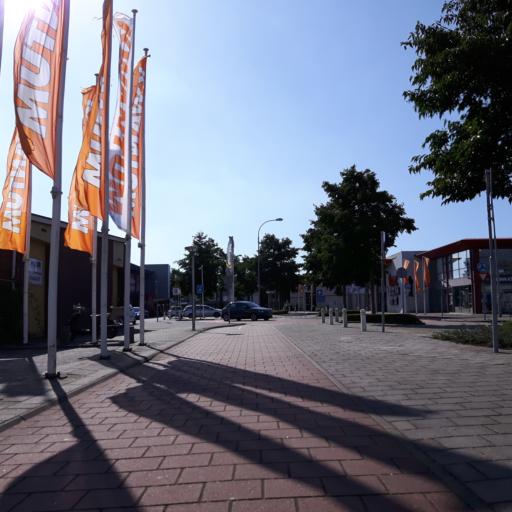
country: NL
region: Zeeland
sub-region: Gemeente Goes
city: Goes
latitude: 51.4993
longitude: 3.8826
